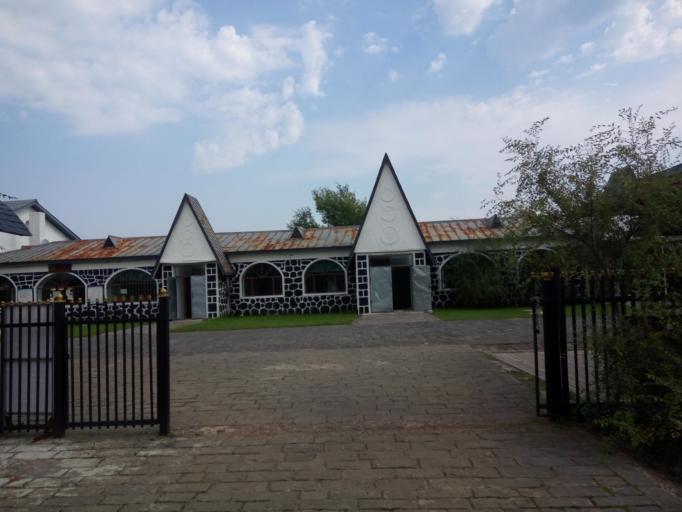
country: CN
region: Heilongjiang Sheng
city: Erjing
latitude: 48.6458
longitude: 126.1491
